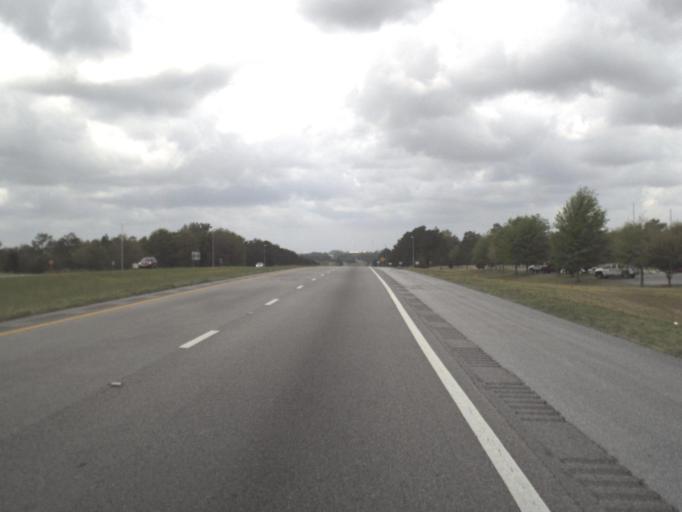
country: US
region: Florida
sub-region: Okaloosa County
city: Crestview
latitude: 30.7270
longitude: -86.5065
